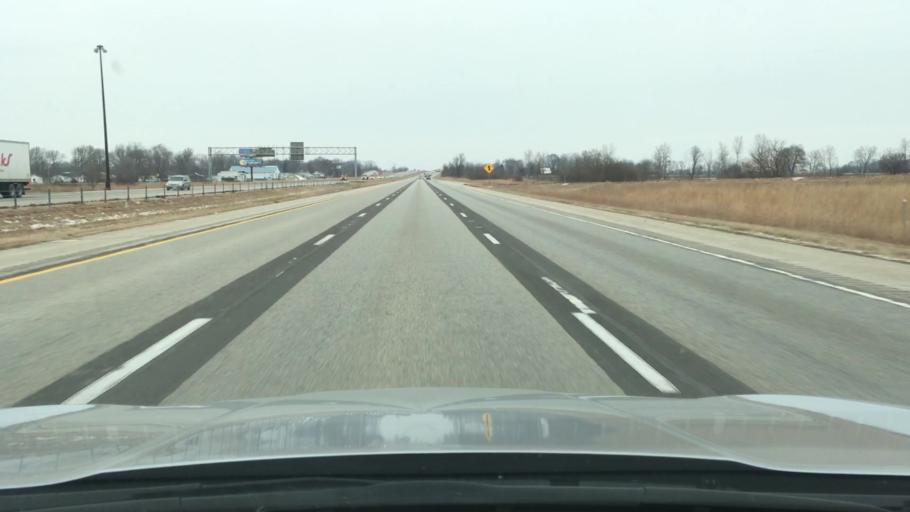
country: US
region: Illinois
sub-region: Sangamon County
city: Divernon
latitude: 39.6179
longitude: -89.6468
